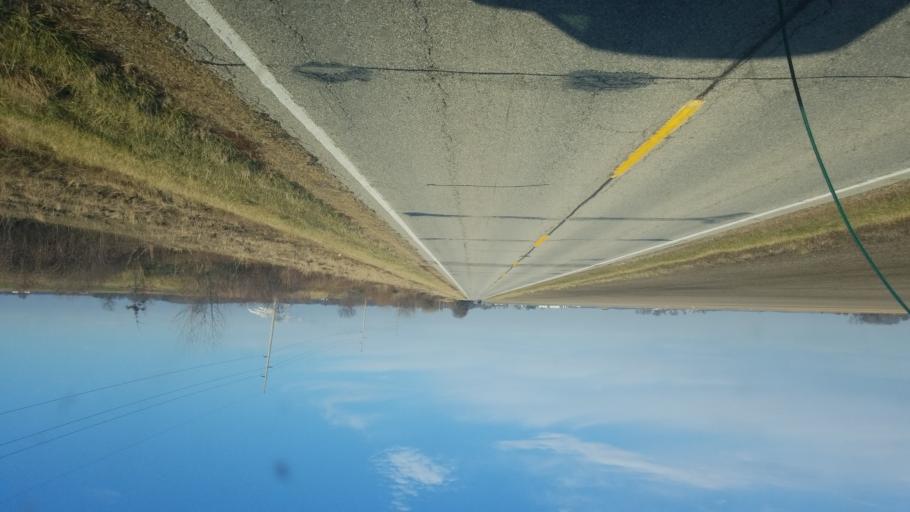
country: US
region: Illinois
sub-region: Edwards County
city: Grayville
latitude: 38.3348
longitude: -87.8973
